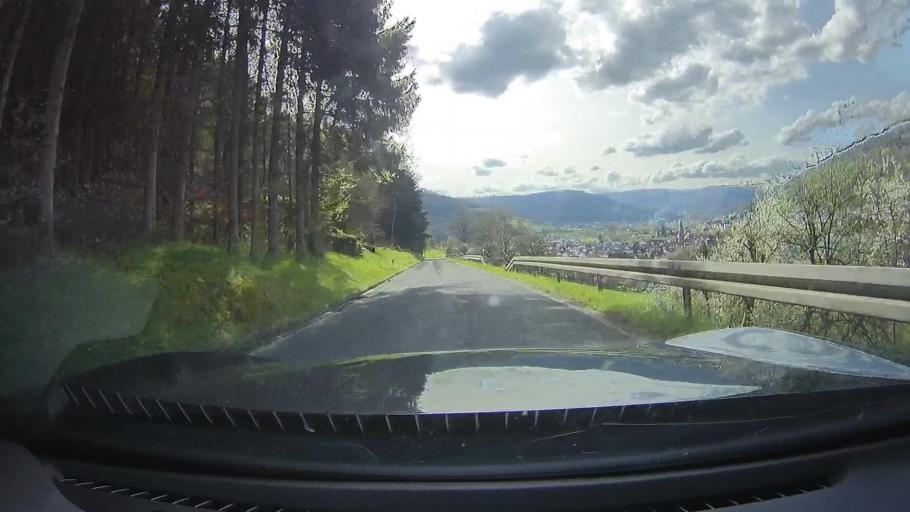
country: DE
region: Bavaria
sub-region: Regierungsbezirk Unterfranken
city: Weilbach
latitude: 49.6388
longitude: 9.2584
